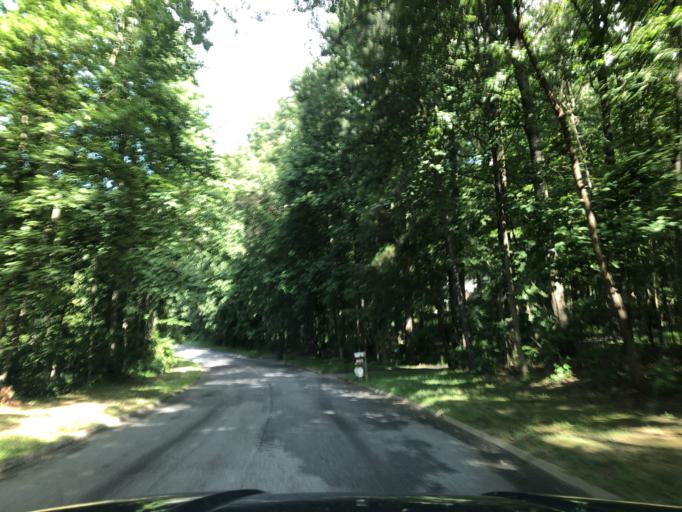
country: US
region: Maryland
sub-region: Howard County
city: Highland
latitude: 39.2110
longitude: -76.9913
